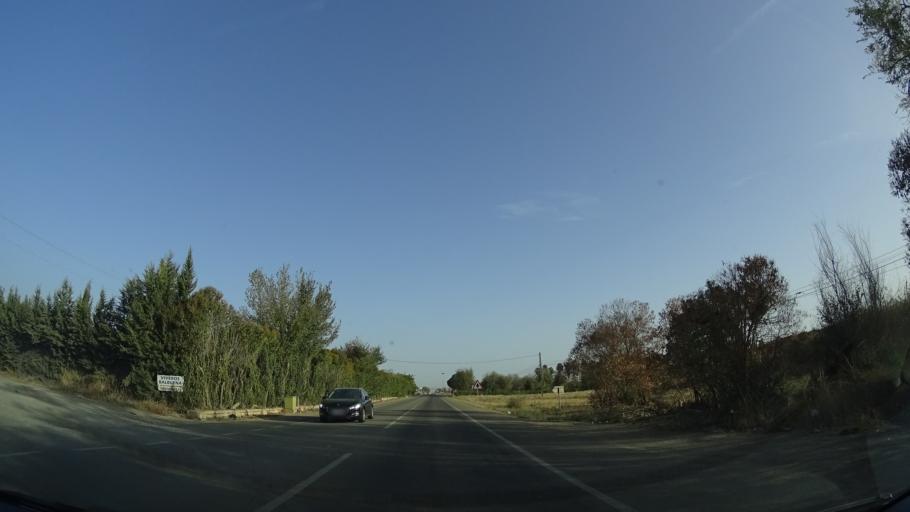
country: ES
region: Andalusia
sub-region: Provincia de Sevilla
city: La Algaba
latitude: 37.4398
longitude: -5.9786
